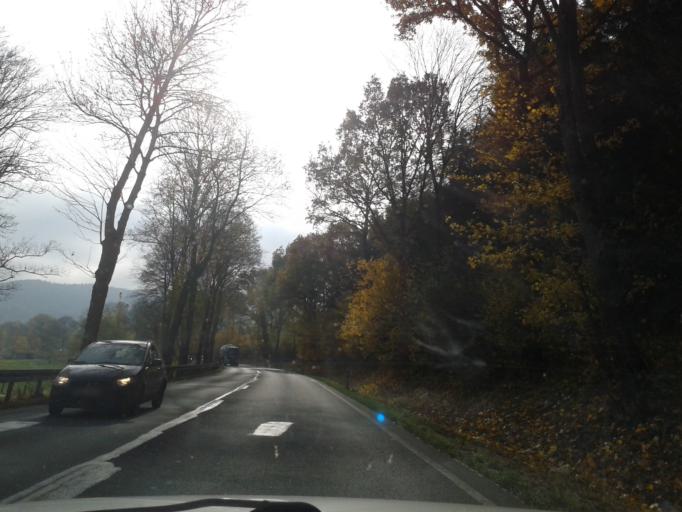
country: DE
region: North Rhine-Westphalia
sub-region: Regierungsbezirk Arnsberg
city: Olsberg
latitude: 51.2995
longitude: 8.4969
